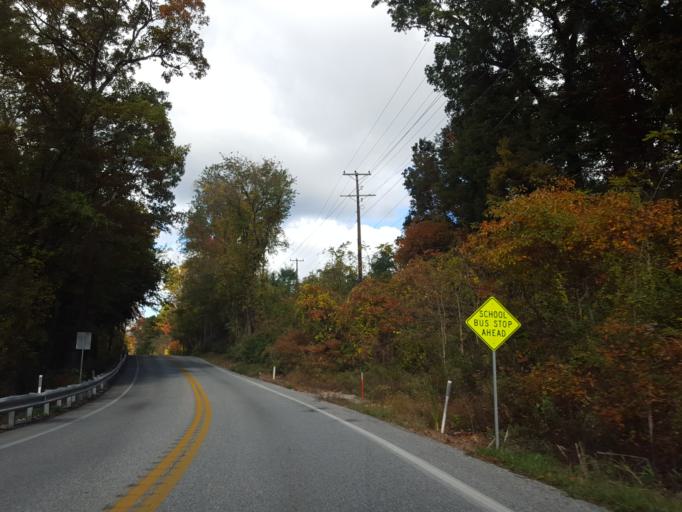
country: US
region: Pennsylvania
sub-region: York County
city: Yoe
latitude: 39.9272
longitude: -76.6500
